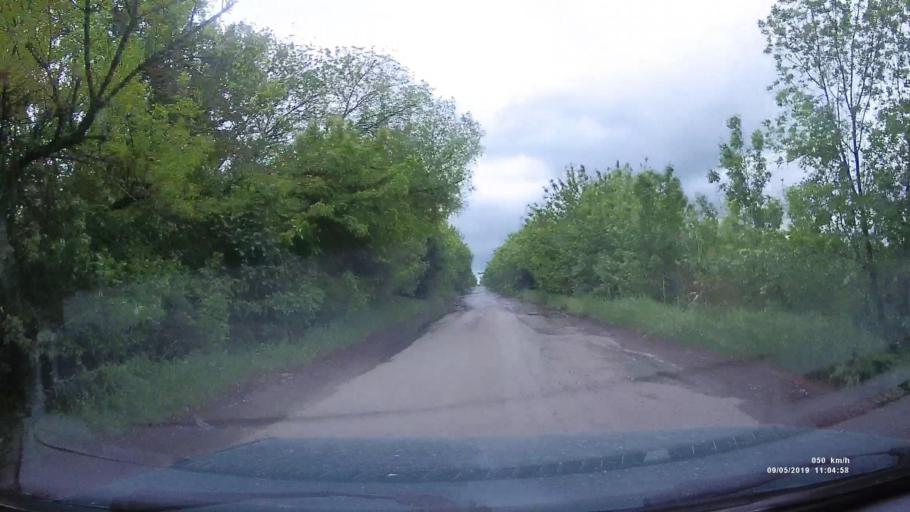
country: RU
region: Krasnodarskiy
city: Kanelovskaya
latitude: 46.8121
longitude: 39.2099
